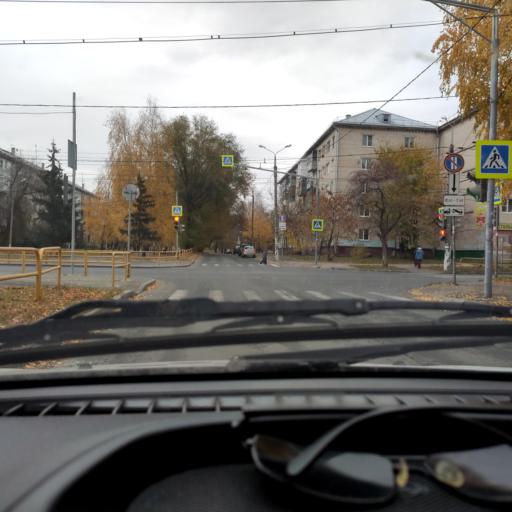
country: RU
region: Samara
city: Tol'yatti
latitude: 53.5161
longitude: 49.4163
